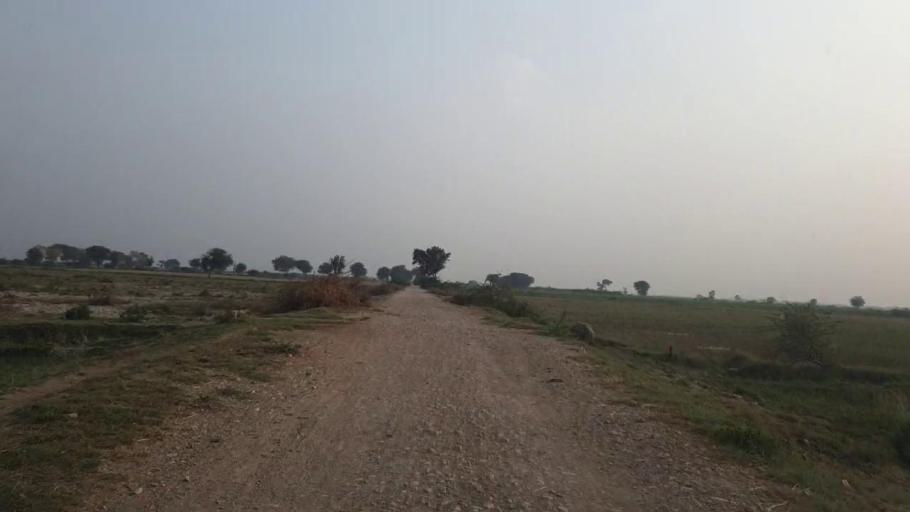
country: PK
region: Sindh
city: Mirpur Batoro
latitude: 24.6545
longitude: 68.3726
